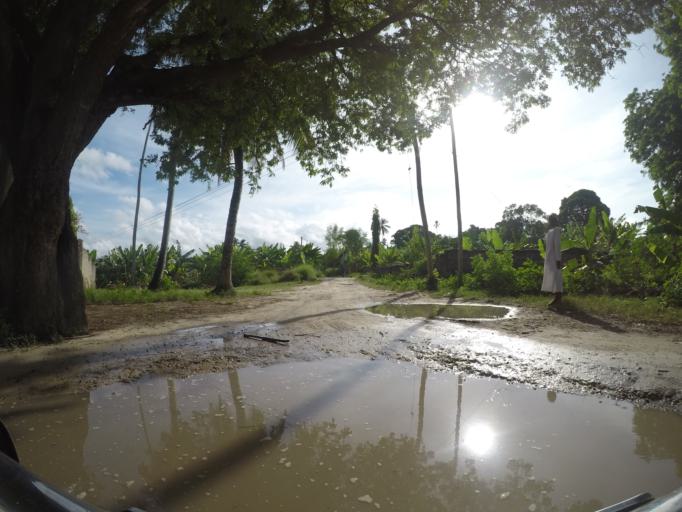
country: TZ
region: Pemba South
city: Chake Chake
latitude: -5.2246
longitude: 39.7781
